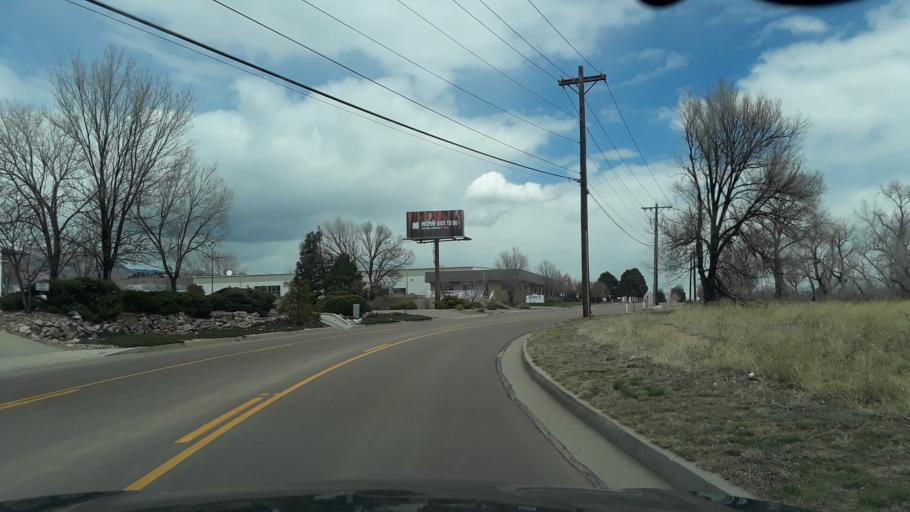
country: US
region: Colorado
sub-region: El Paso County
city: Colorado Springs
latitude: 38.8910
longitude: -104.8256
